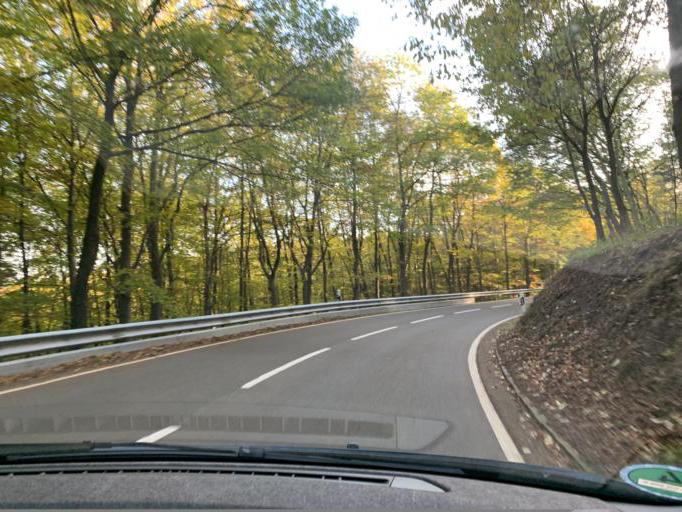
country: DE
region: North Rhine-Westphalia
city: Heimbach
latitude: 50.6151
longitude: 6.4808
